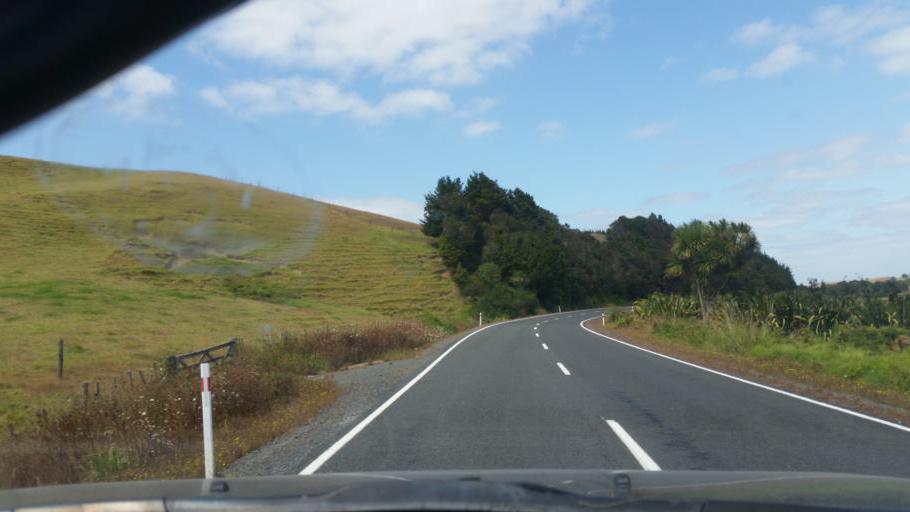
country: NZ
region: Northland
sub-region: Whangarei
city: Ruakaka
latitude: -35.9658
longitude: 174.2913
